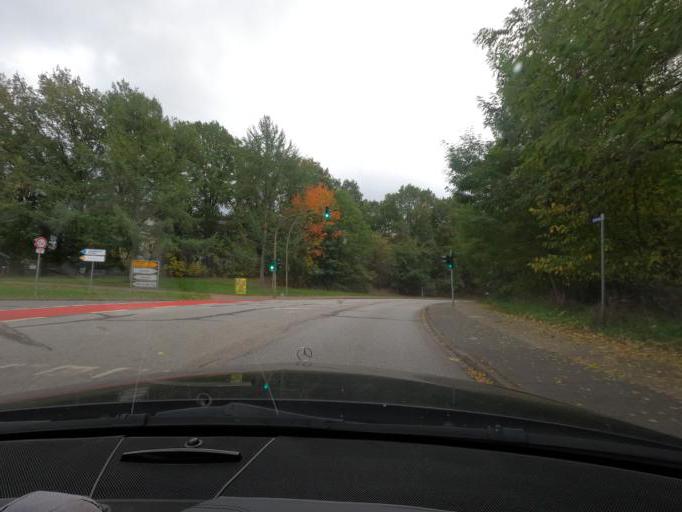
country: DE
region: Schleswig-Holstein
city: Geesthacht
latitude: 53.4463
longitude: 10.3746
